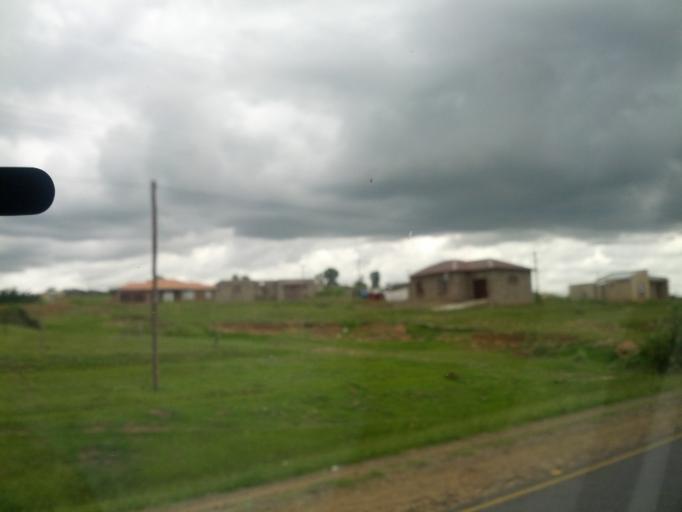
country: LS
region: Berea
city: Teyateyaneng
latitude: -29.1105
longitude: 27.7530
